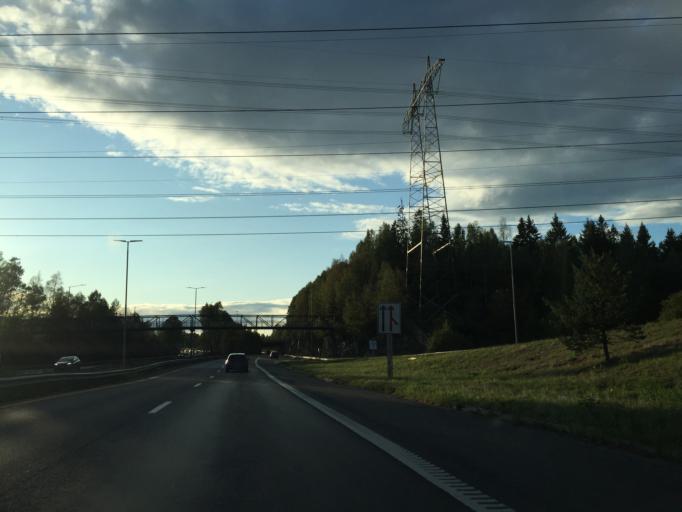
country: NO
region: Akershus
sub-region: Lorenskog
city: Kjenn
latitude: 59.9371
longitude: 10.9347
